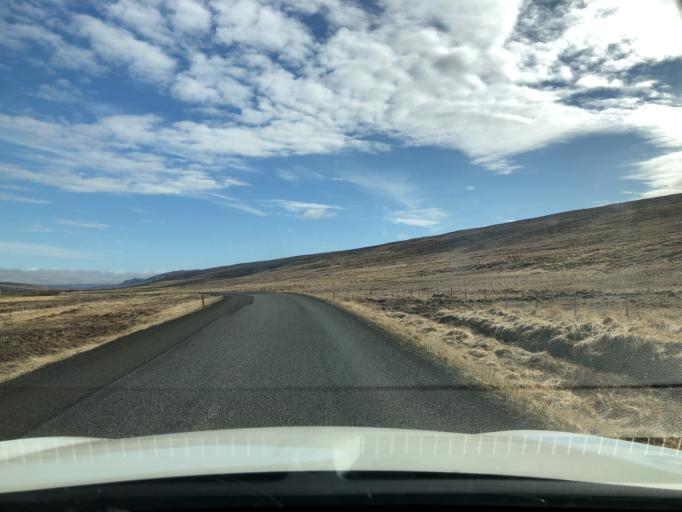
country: IS
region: West
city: Borgarnes
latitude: 65.0912
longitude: -21.7333
